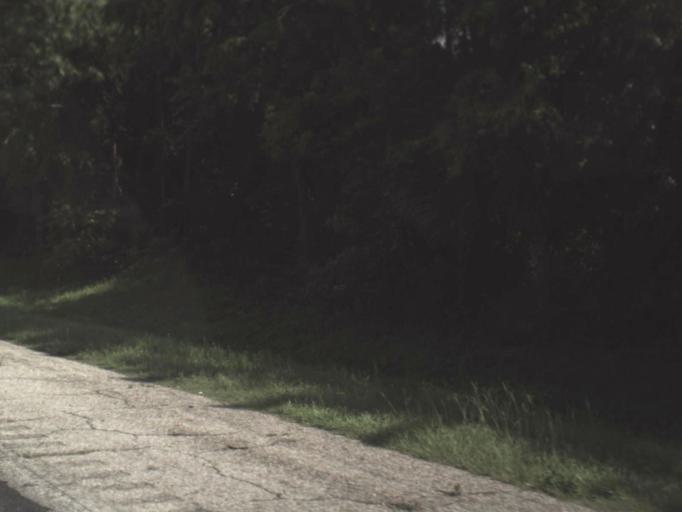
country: US
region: Florida
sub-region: Alachua County
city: Gainesville
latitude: 29.6505
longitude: -82.4110
